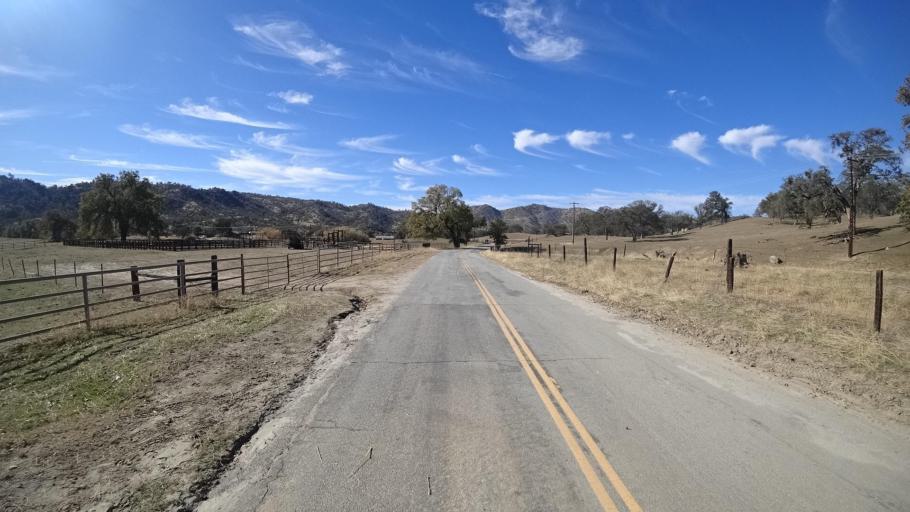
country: US
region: California
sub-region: Kern County
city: Alta Sierra
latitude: 35.6184
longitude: -118.7286
